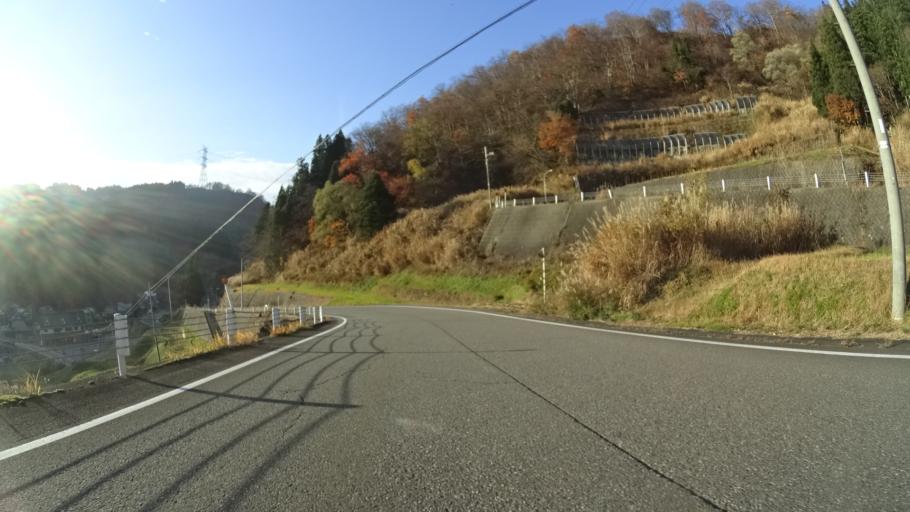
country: JP
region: Niigata
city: Shiozawa
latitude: 36.9860
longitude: 138.7465
